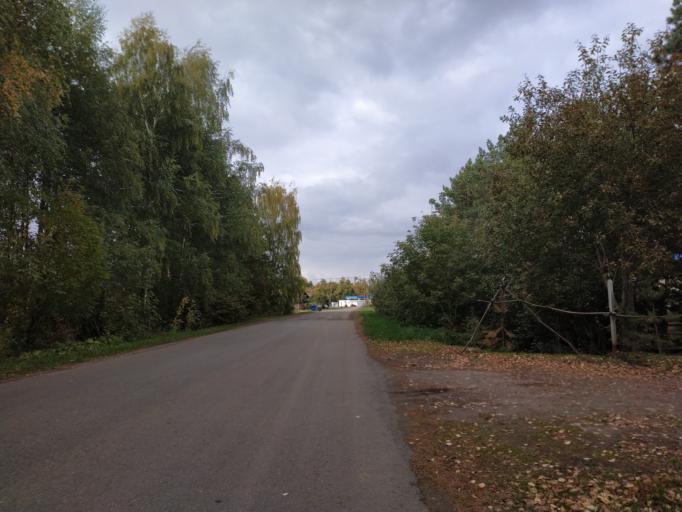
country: RU
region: Chuvashia
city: Ishley
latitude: 56.1306
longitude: 47.0882
